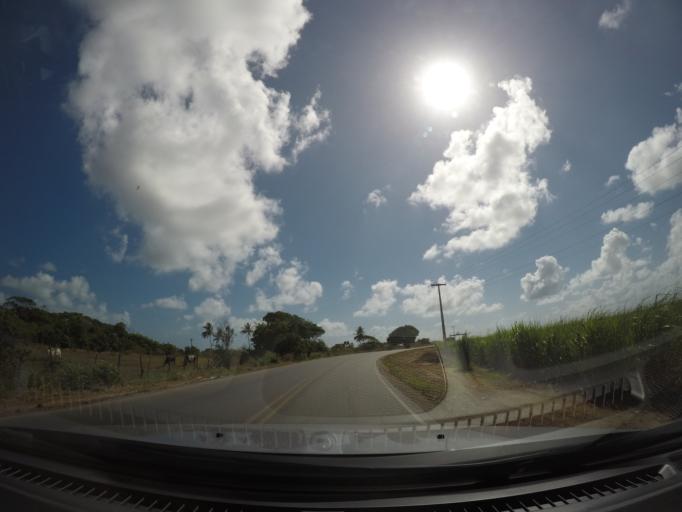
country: BR
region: Paraiba
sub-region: Pitimbu
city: Pitimbu
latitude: -7.4718
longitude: -34.8234
